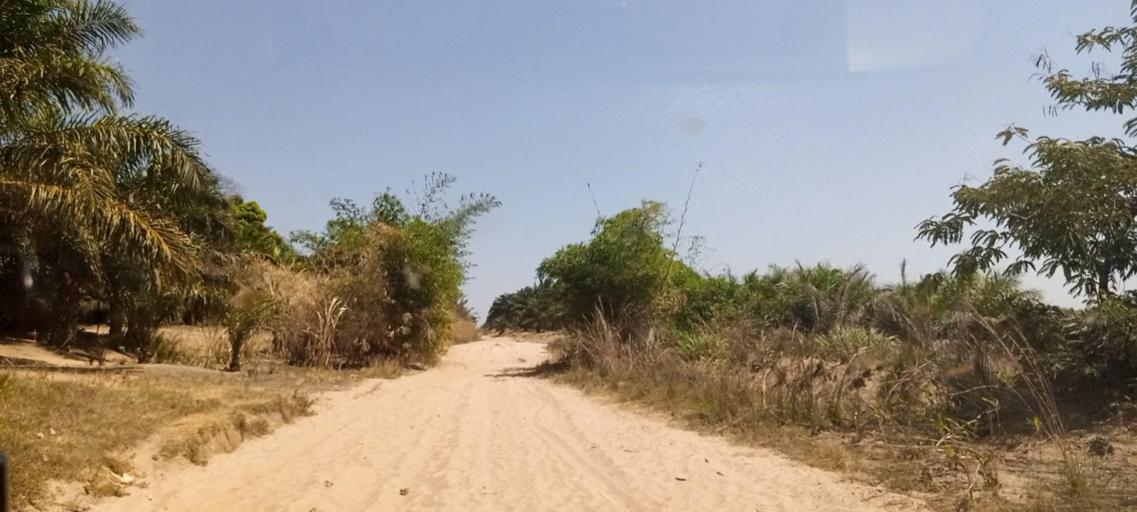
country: CD
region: Kasai-Oriental
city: Kabinda
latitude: -5.9593
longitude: 24.7892
